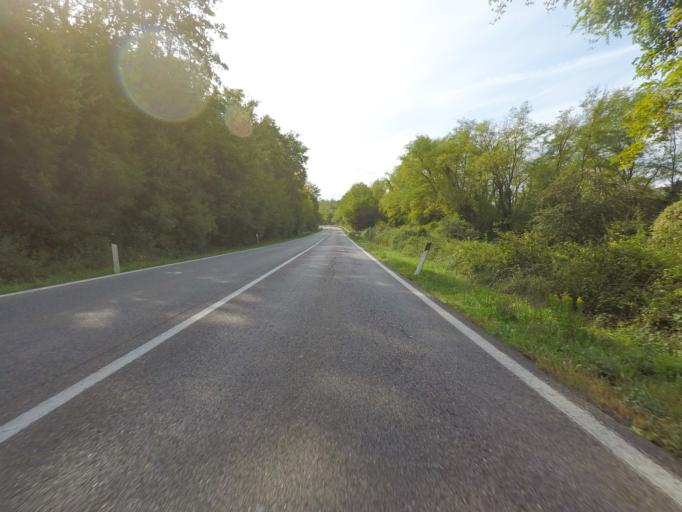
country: IT
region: Tuscany
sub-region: Provincia di Siena
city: Rosia
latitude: 43.1899
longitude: 11.2775
